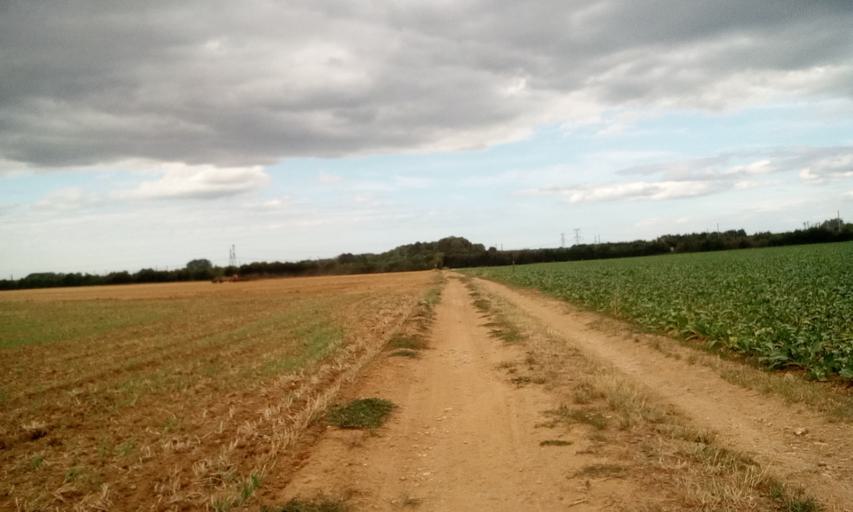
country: FR
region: Lower Normandy
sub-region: Departement du Calvados
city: Bellengreville
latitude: 49.1226
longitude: -0.2240
